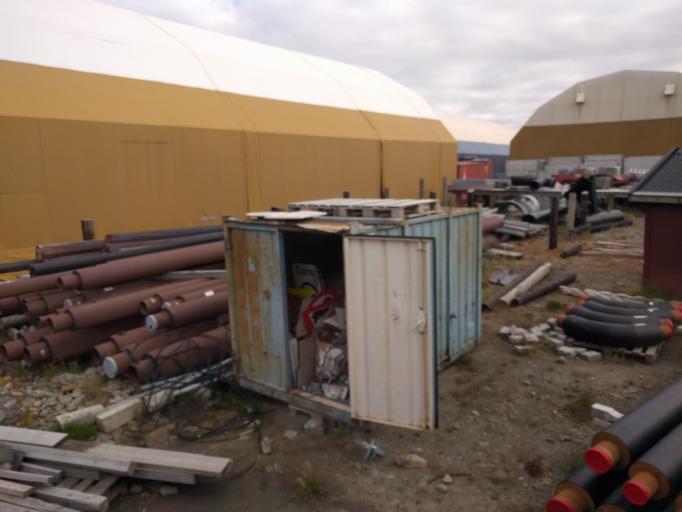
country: SJ
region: Svalbard
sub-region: Spitsbergen
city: Longyearbyen
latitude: 78.2231
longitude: 15.6335
